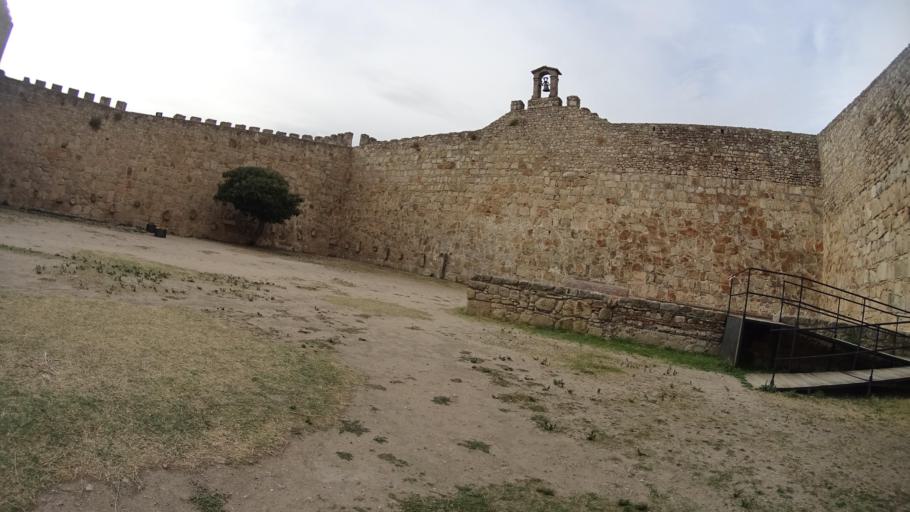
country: ES
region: Extremadura
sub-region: Provincia de Caceres
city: Trujillo
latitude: 39.4624
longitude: -5.8823
